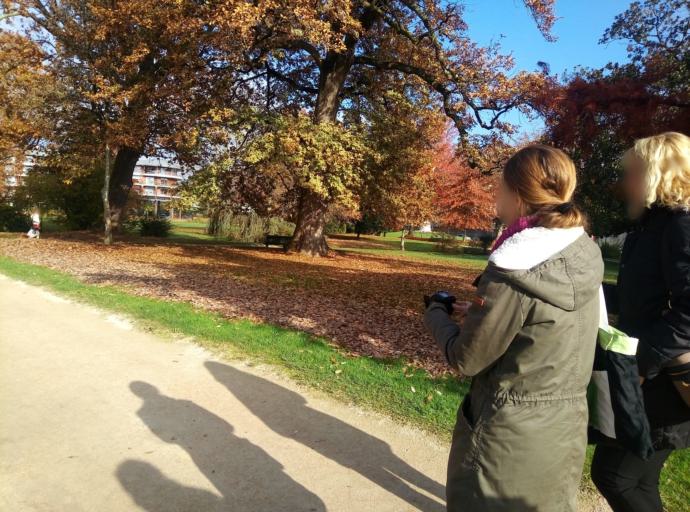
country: FR
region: Aquitaine
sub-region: Departement des Pyrenees-Atlantiques
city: Pau
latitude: 43.2959
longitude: -0.3604
